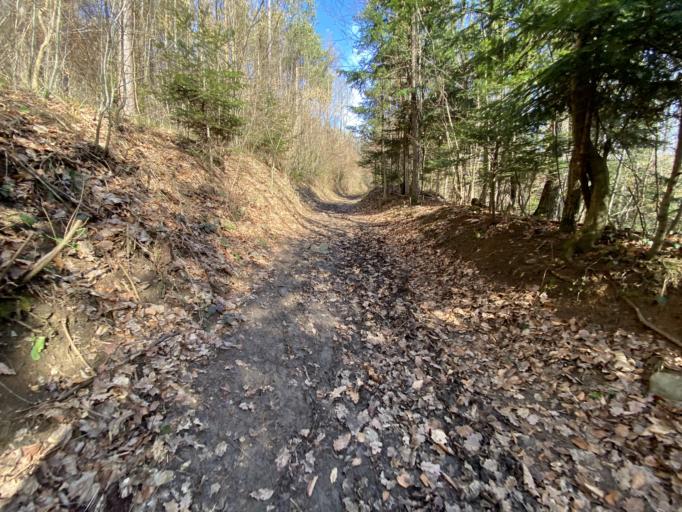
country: AT
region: Lower Austria
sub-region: Politischer Bezirk Modling
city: Gaaden
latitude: 48.0160
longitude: 16.1617
